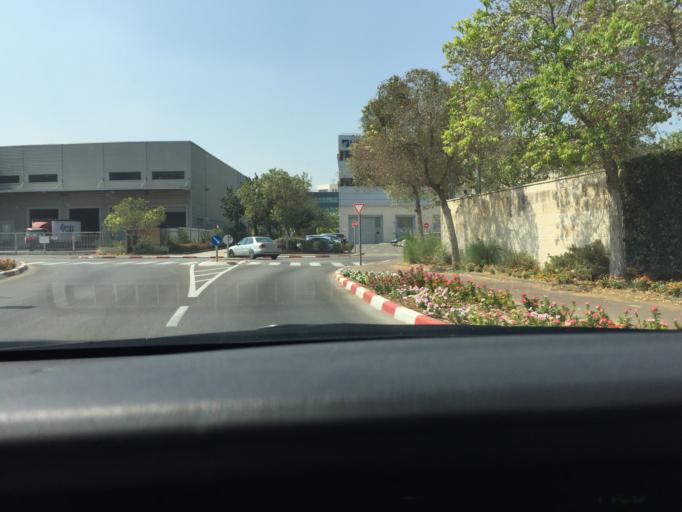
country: IL
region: Central District
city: Lod
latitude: 31.9894
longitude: 34.9144
